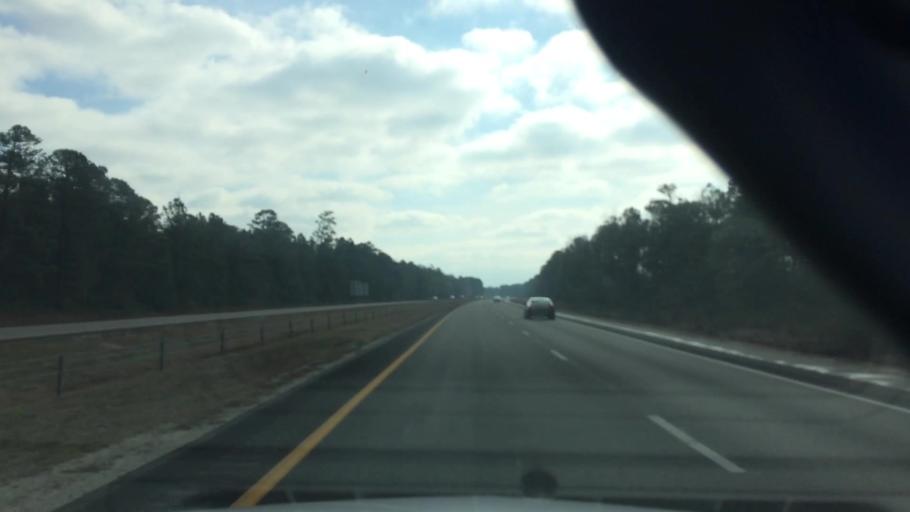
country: US
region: North Carolina
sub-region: Pender County
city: Burgaw
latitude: 34.5483
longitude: -77.8935
